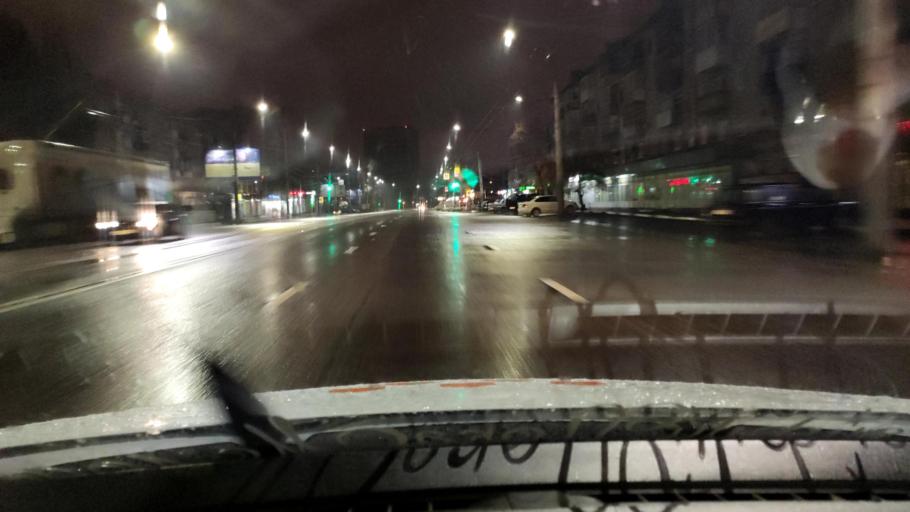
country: RU
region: Voronezj
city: Voronezh
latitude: 51.6697
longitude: 39.2512
